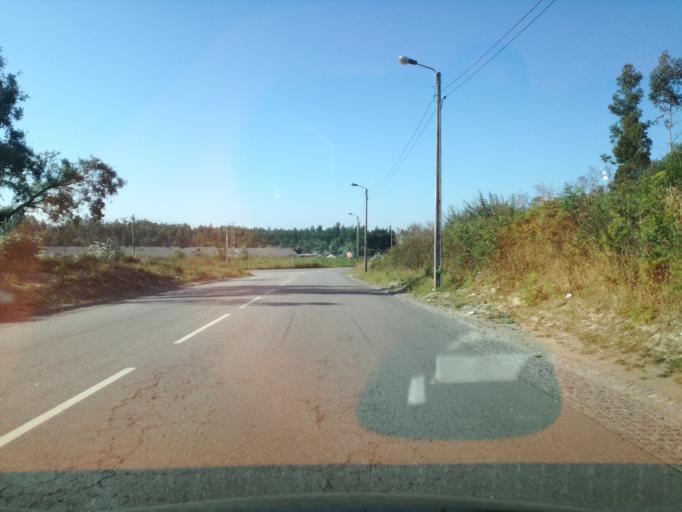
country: PT
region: Porto
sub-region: Maia
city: Nogueira
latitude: 41.2568
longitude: -8.5736
